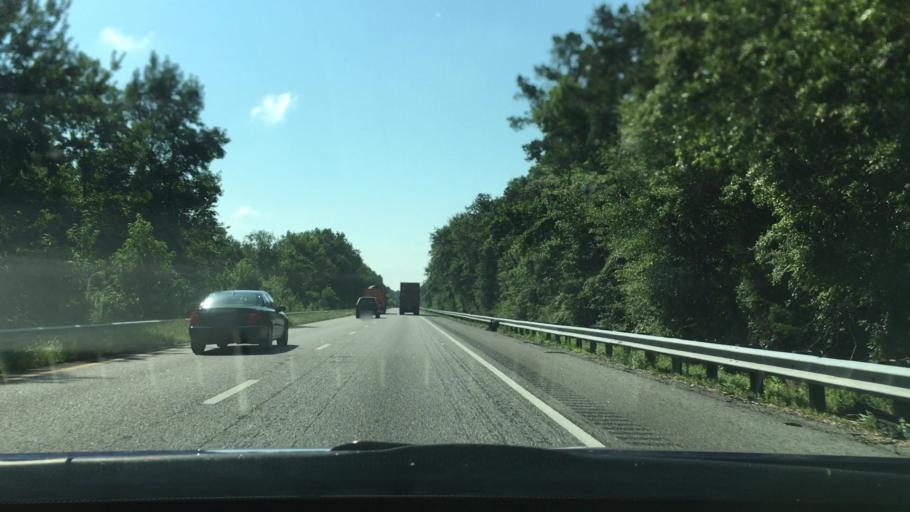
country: US
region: South Carolina
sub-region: Dorchester County
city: Ridgeville
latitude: 33.1497
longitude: -80.3367
